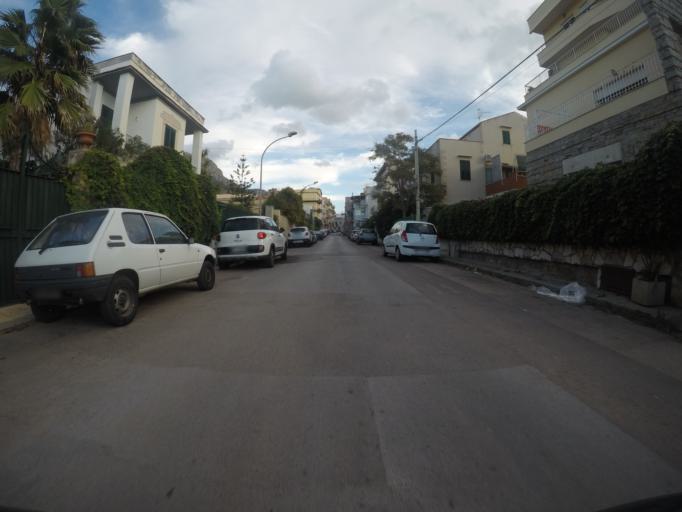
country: IT
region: Sicily
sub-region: Palermo
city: Isola delle Femmine
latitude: 38.2013
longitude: 13.2772
